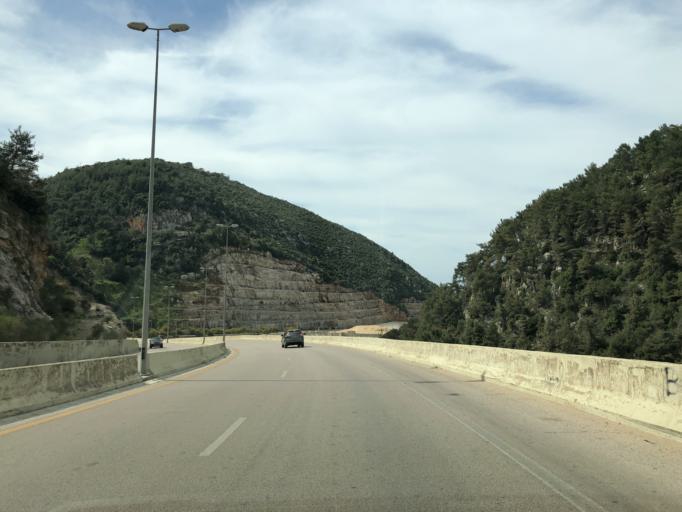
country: LB
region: Mont-Liban
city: Bhamdoun el Mhatta
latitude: 33.8955
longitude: 35.6543
